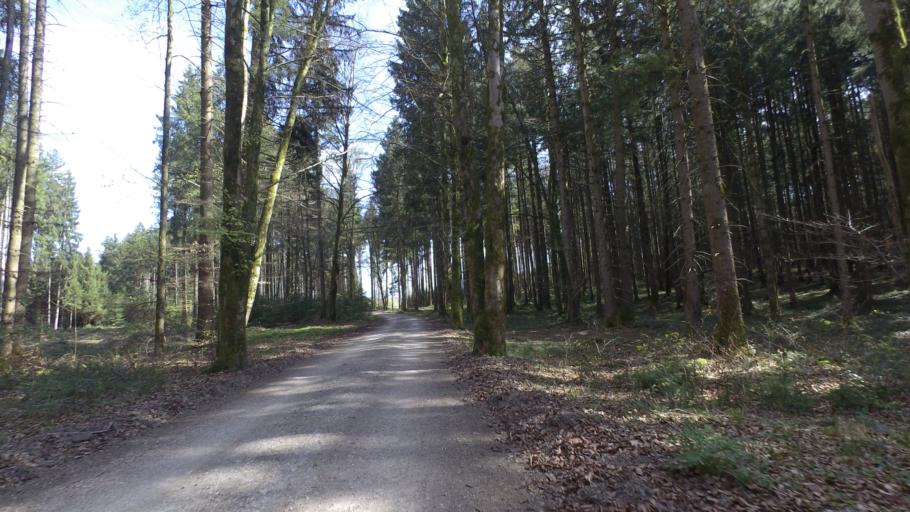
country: DE
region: Bavaria
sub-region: Upper Bavaria
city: Nussdorf
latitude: 47.9164
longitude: 12.5795
